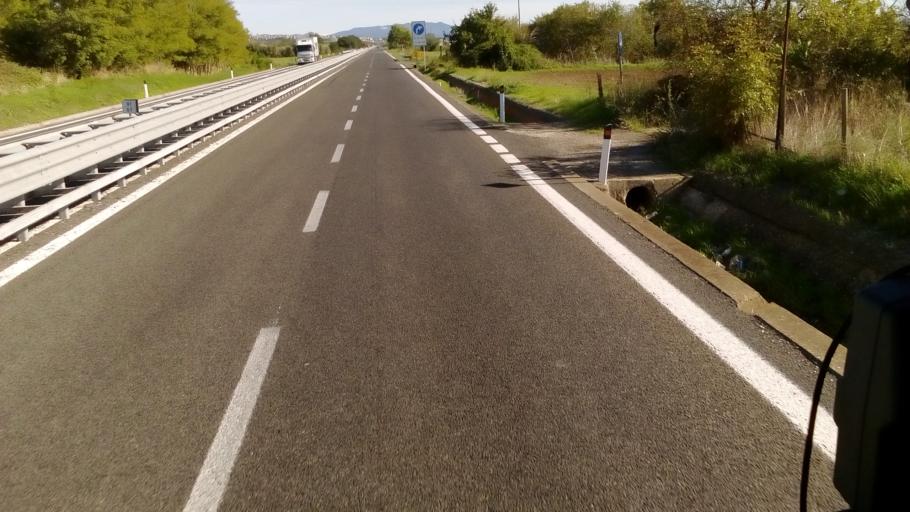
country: IT
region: Latium
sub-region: Provincia di Viterbo
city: Tarquinia
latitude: 42.2806
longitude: 11.6959
